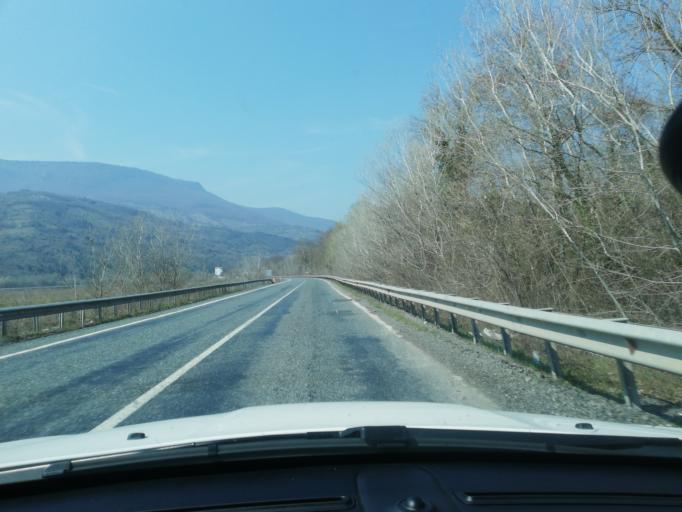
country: TR
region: Karabuk
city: Yenice
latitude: 41.2154
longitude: 32.2814
